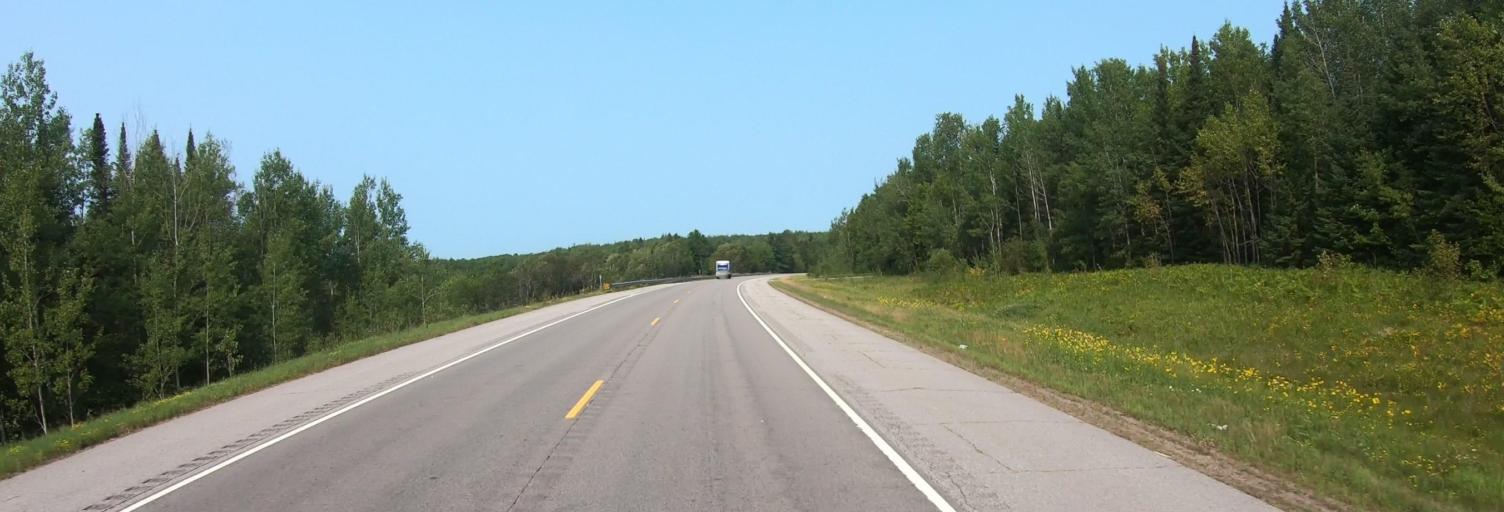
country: CA
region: Ontario
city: Fort Frances
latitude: 48.2193
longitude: -92.9169
